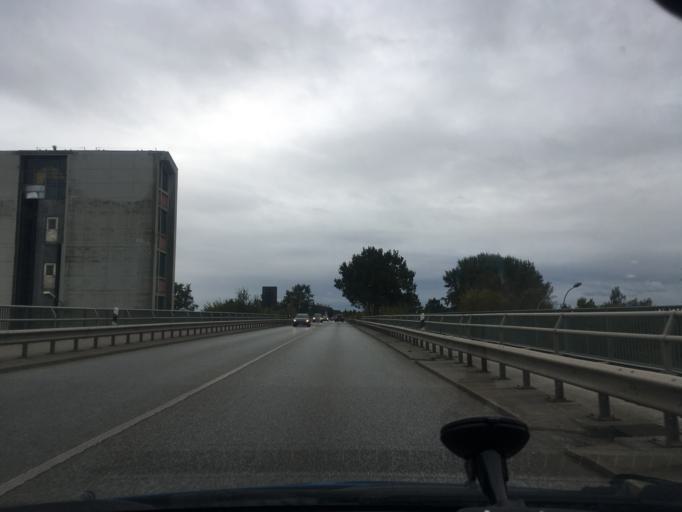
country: DE
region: Schleswig-Holstein
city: Escheburg
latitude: 53.4327
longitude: 10.3362
